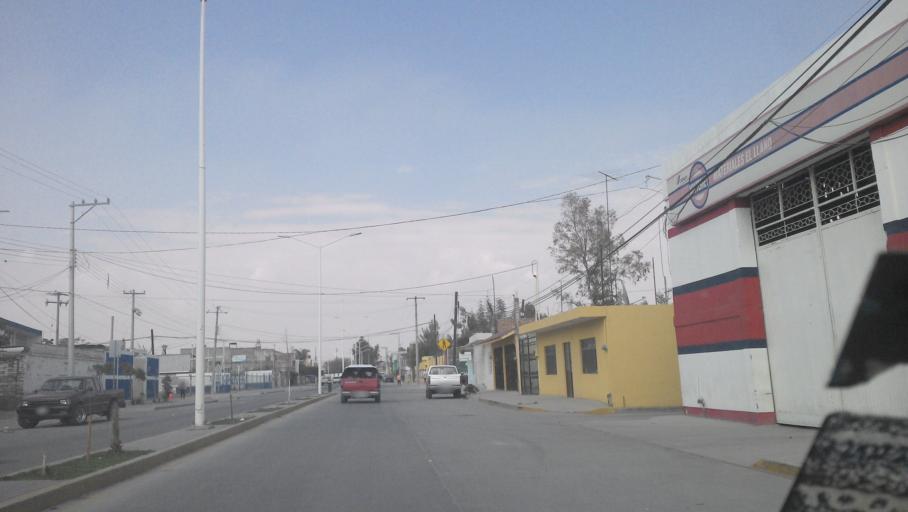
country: MX
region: Guanajuato
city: San Francisco del Rincon
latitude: 21.0059
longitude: -101.8517
